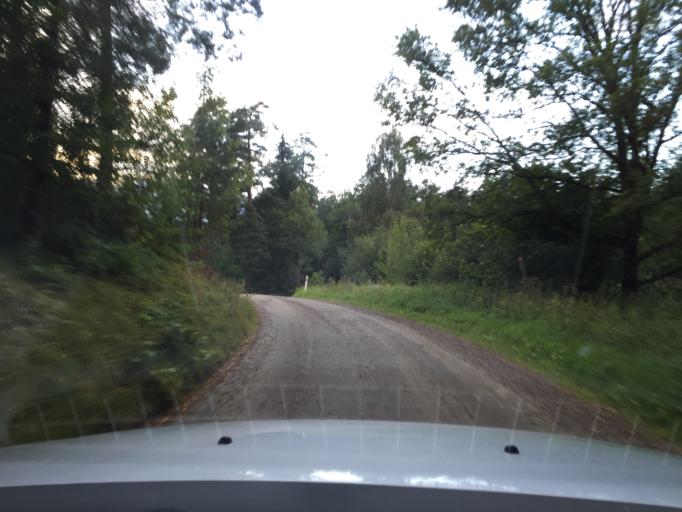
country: SE
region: Skane
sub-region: Hassleholms Kommun
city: Sosdala
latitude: 56.0572
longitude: 13.6661
